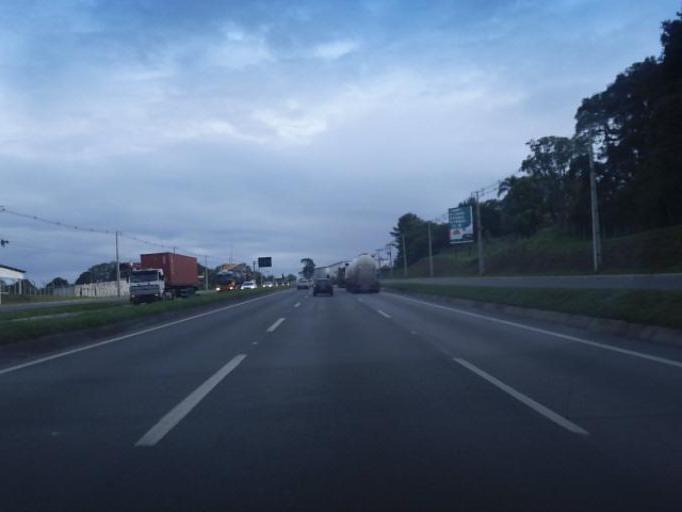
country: BR
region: Parana
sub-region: Sao Jose Dos Pinhais
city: Sao Jose dos Pinhais
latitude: -25.5794
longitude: -49.1783
